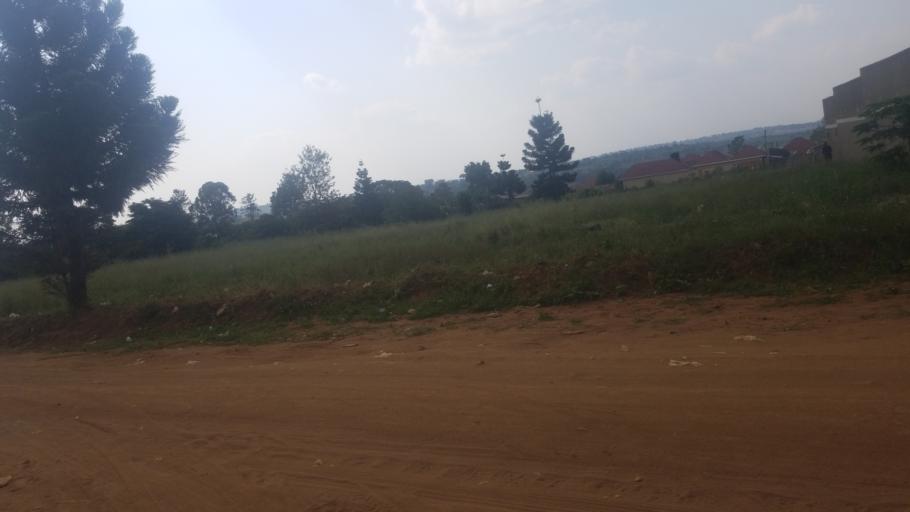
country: UG
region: Central Region
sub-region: Sembabule District
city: Sembabule
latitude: -0.0823
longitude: 31.4580
